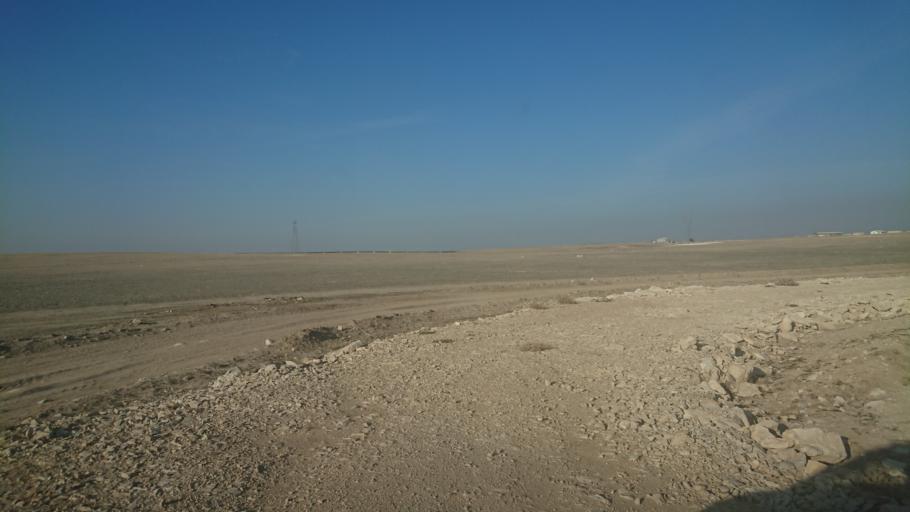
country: TR
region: Aksaray
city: Sultanhani
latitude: 38.1412
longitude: 33.5722
